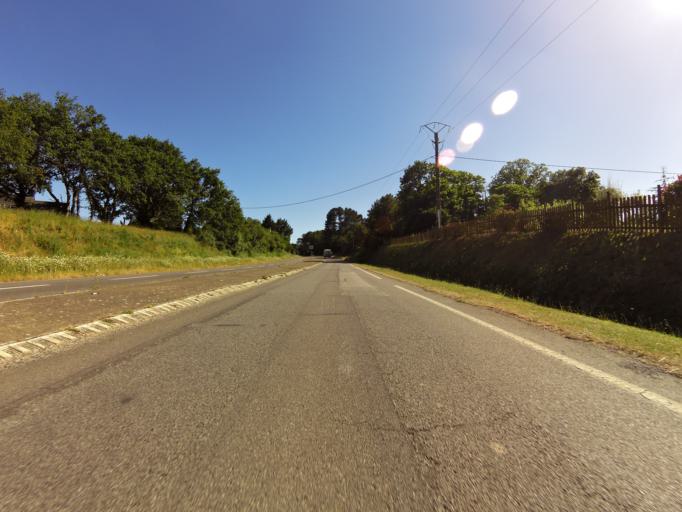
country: FR
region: Brittany
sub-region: Departement du Morbihan
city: Ferel
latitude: 47.4939
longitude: -2.3877
